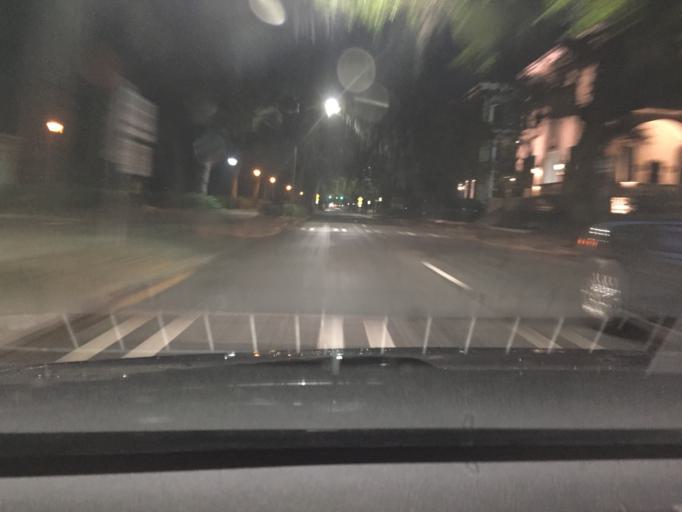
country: US
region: Georgia
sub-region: Chatham County
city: Savannah
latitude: 32.0678
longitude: -81.0949
